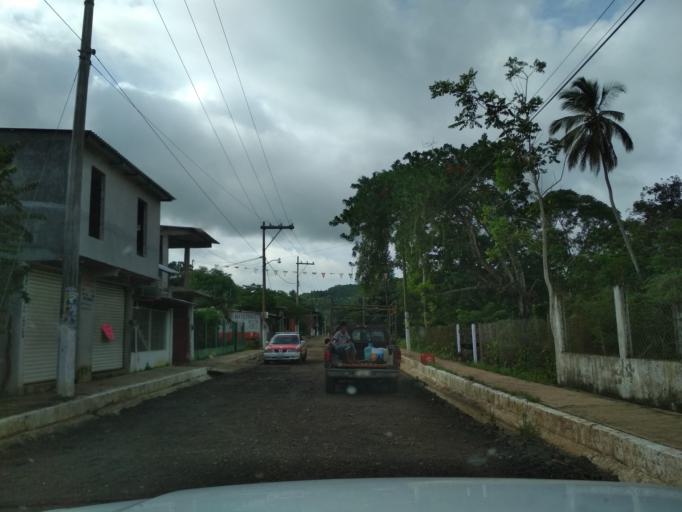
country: MX
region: Veracruz
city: Catemaco
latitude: 18.3750
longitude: -95.1226
